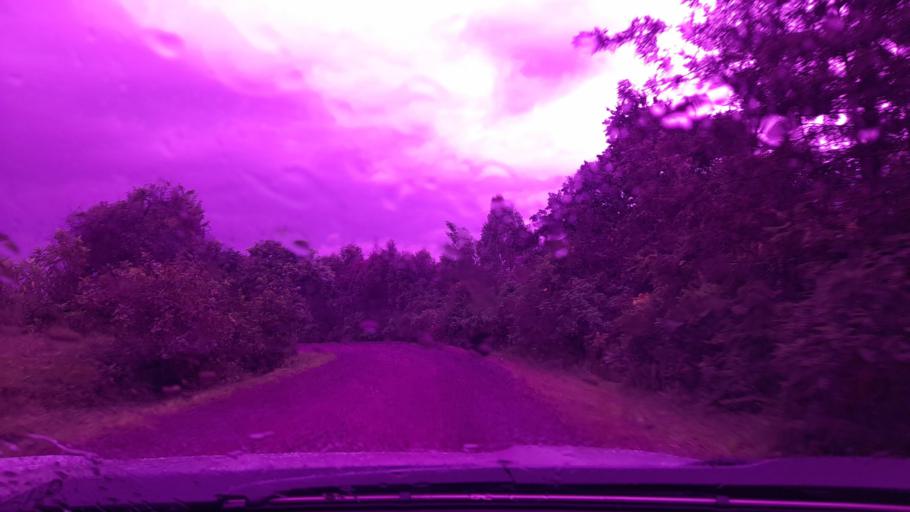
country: ET
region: Oromiya
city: Metu
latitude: 8.4333
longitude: 35.6156
